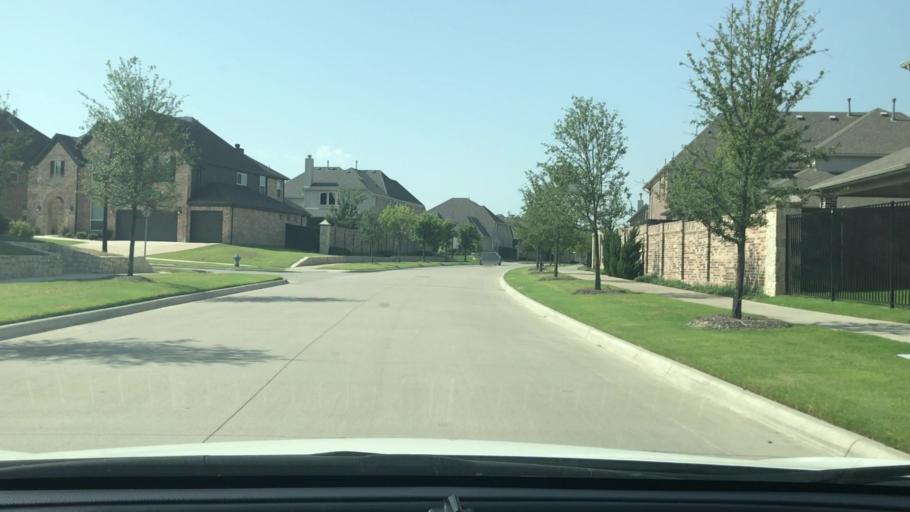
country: US
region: Texas
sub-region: Collin County
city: Frisco
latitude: 33.1325
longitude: -96.7648
